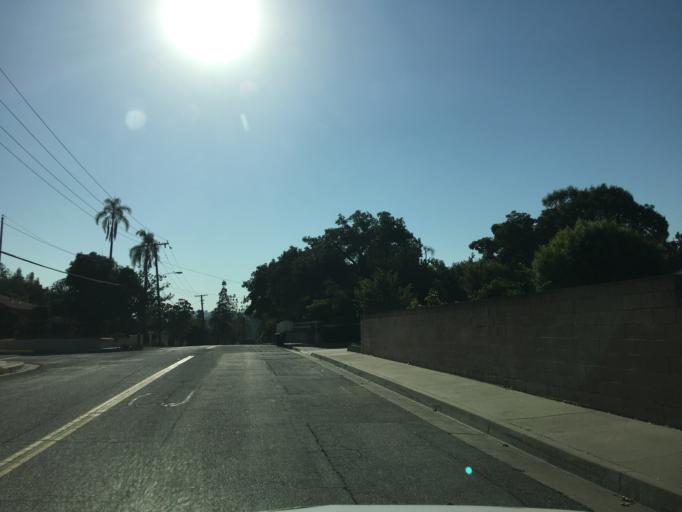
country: US
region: California
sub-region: Los Angeles County
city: Charter Oak
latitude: 34.0862
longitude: -117.8527
